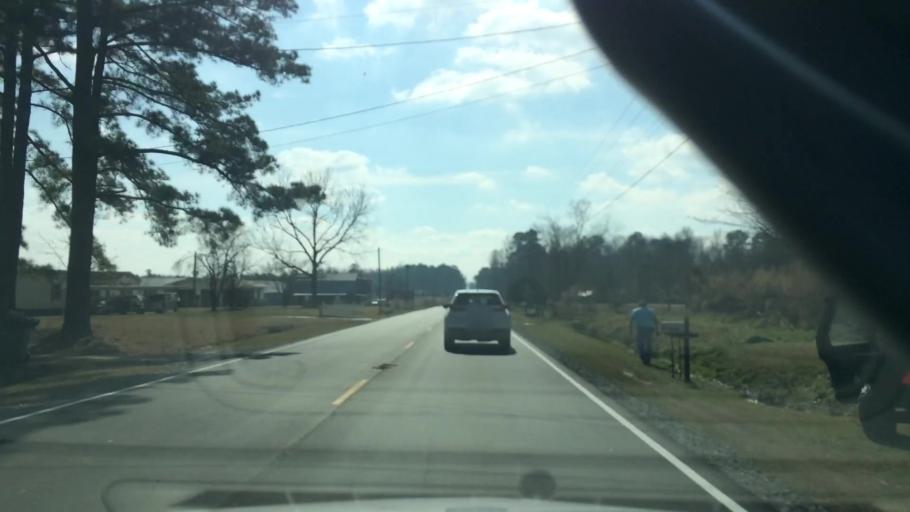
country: US
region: North Carolina
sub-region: Duplin County
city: Beulaville
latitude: 34.9710
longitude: -77.7622
